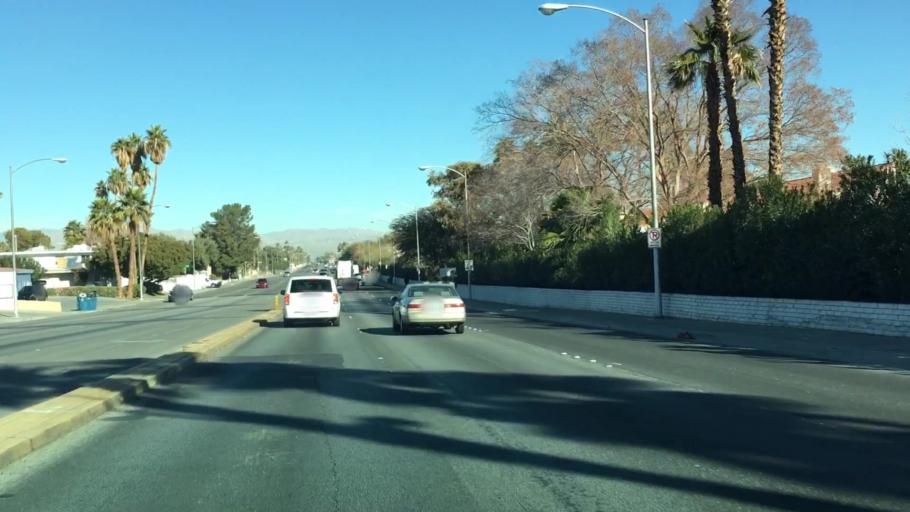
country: US
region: Nevada
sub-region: Clark County
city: Winchester
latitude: 36.1188
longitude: -115.1190
